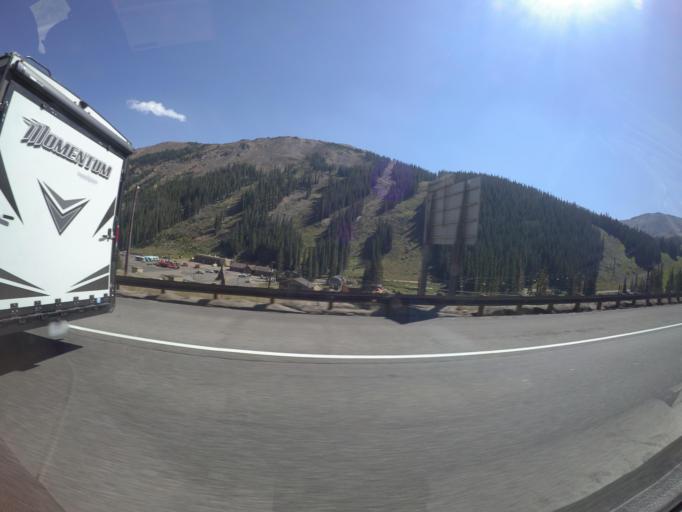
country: US
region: Colorado
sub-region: Summit County
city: Keystone
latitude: 39.6817
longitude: -105.8992
